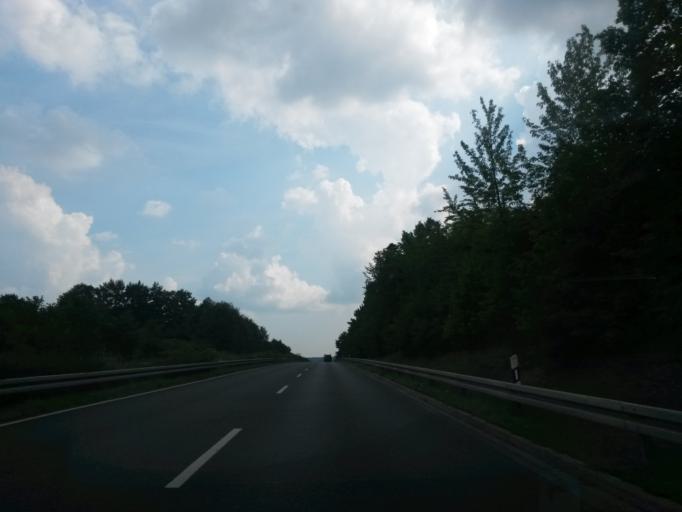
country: DE
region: Bavaria
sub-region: Regierungsbezirk Mittelfranken
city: Zirndorf
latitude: 49.4501
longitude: 10.9752
